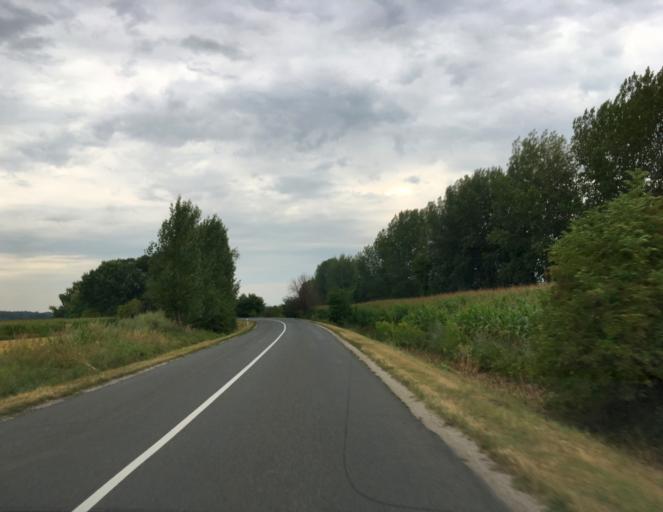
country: SK
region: Trnavsky
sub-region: Okres Dunajska Streda
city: Velky Meder
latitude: 47.9034
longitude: 17.6803
